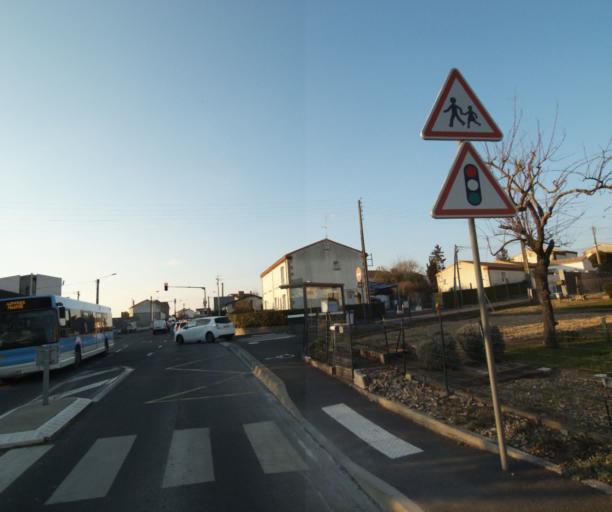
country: FR
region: Poitou-Charentes
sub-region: Departement des Deux-Sevres
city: Niort
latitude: 46.3108
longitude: -0.4458
